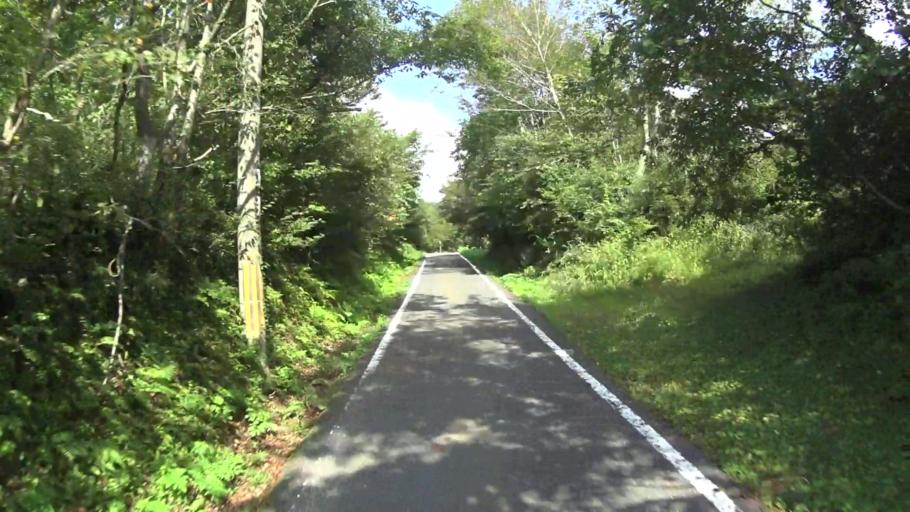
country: JP
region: Kyoto
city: Miyazu
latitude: 35.6467
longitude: 135.1805
